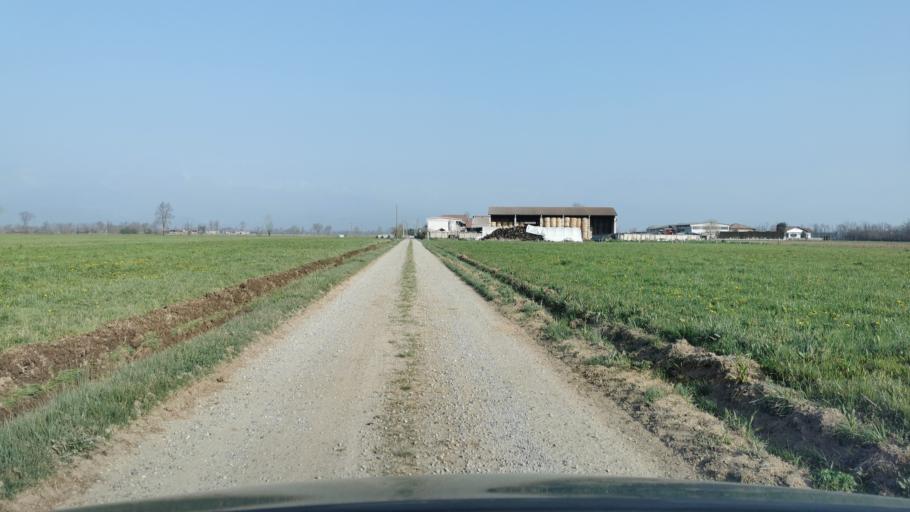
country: IT
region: Piedmont
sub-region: Provincia di Torino
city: Rivarossa
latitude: 45.2650
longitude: 7.7294
